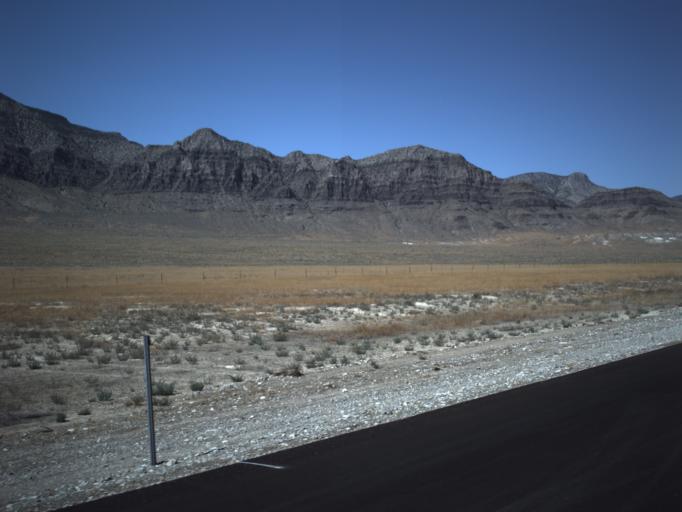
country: US
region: Utah
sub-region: Beaver County
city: Milford
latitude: 39.0717
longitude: -113.4650
